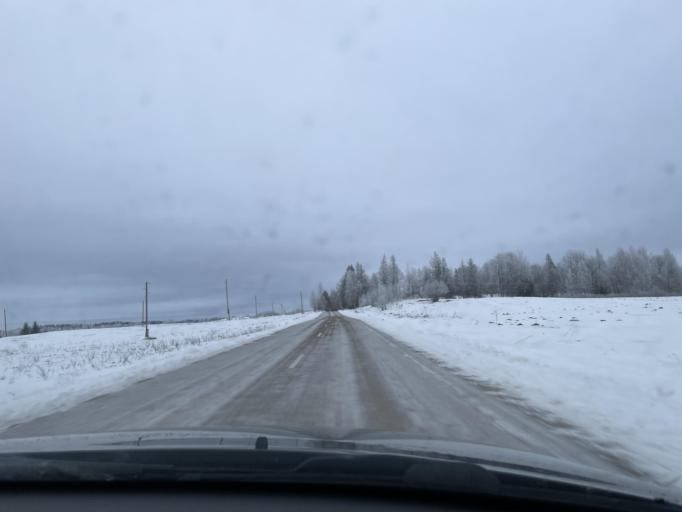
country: LV
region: Ludzas Rajons
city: Ludza
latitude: 56.4517
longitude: 27.5531
